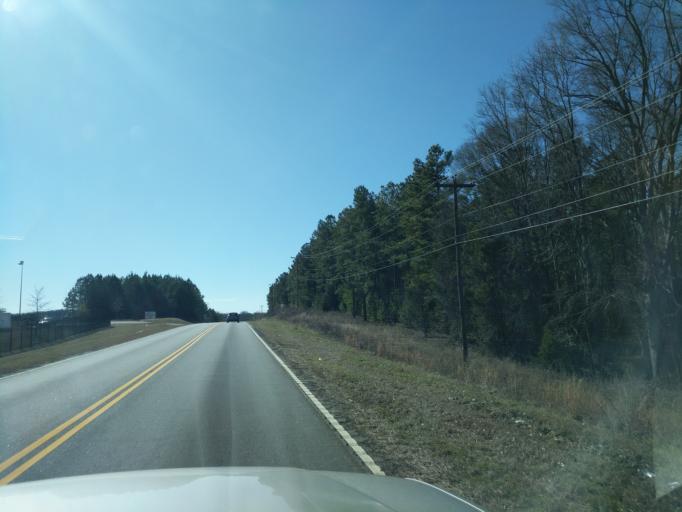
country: US
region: South Carolina
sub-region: Anderson County
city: Homeland Park
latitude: 34.4605
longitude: -82.6895
